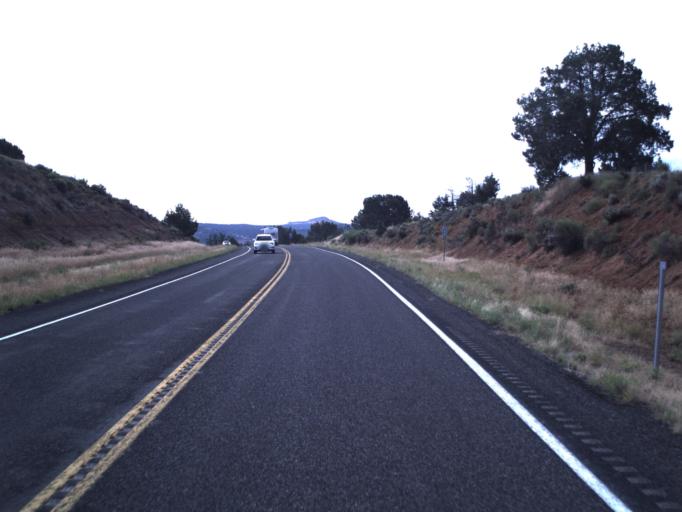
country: US
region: Utah
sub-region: Kane County
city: Kanab
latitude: 37.2282
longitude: -112.7279
